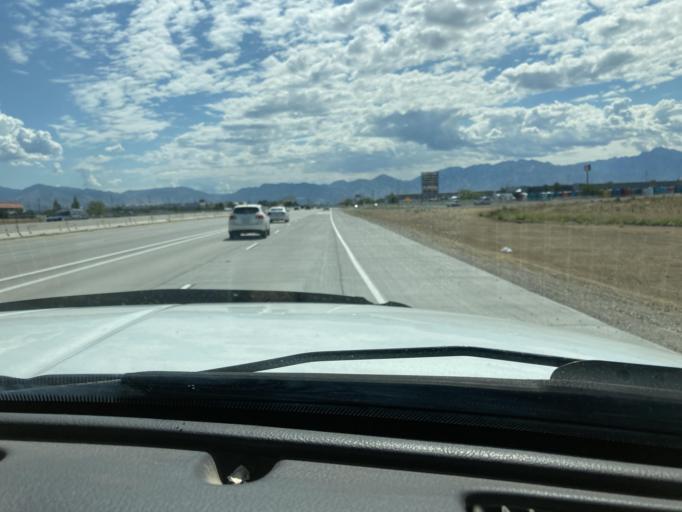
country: US
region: Utah
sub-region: Salt Lake County
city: West Valley City
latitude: 40.7256
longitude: -112.0235
